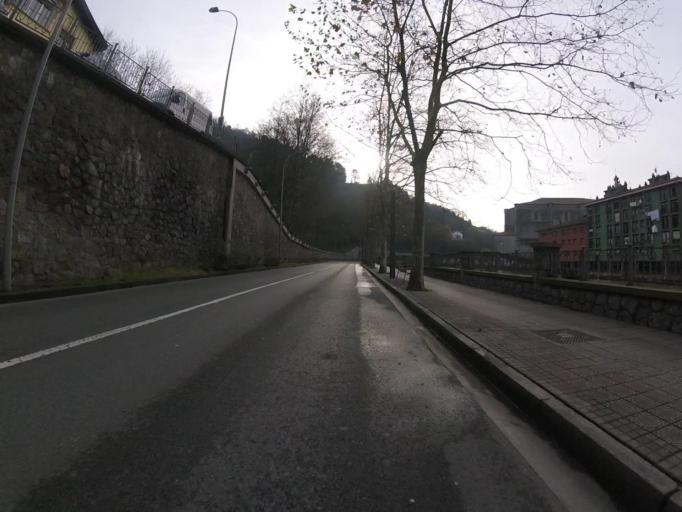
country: ES
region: Basque Country
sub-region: Provincia de Guipuzcoa
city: Tolosa
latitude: 43.1396
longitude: -2.0705
